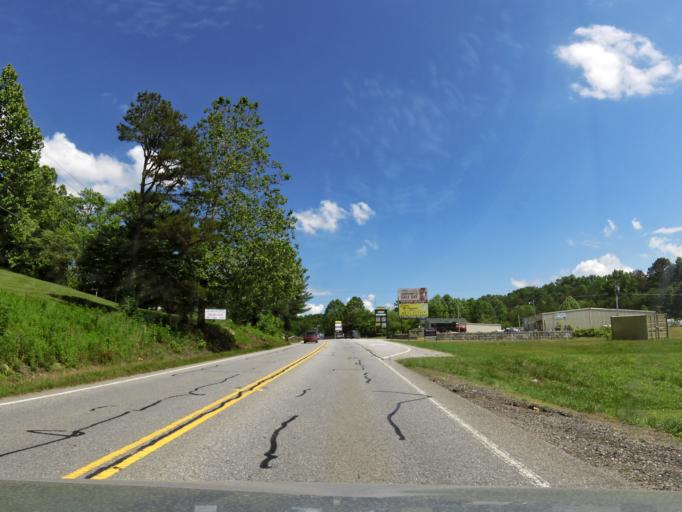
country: US
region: Georgia
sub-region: Union County
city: Blairsville
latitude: 34.8821
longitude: -83.9840
